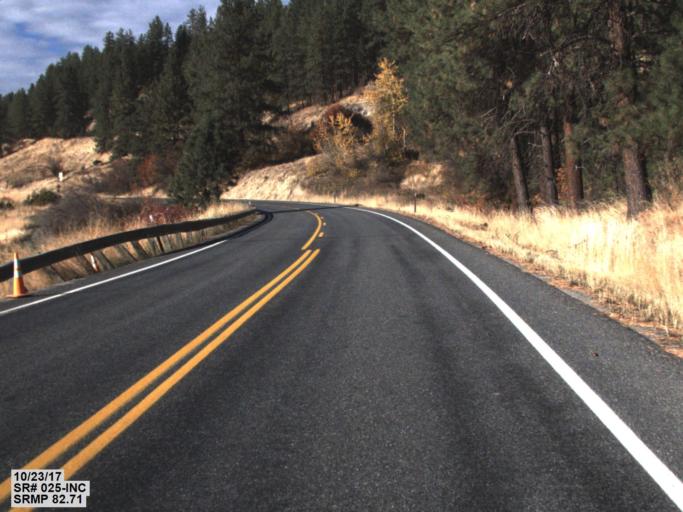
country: US
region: Washington
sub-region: Stevens County
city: Kettle Falls
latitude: 48.6279
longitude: -118.0736
